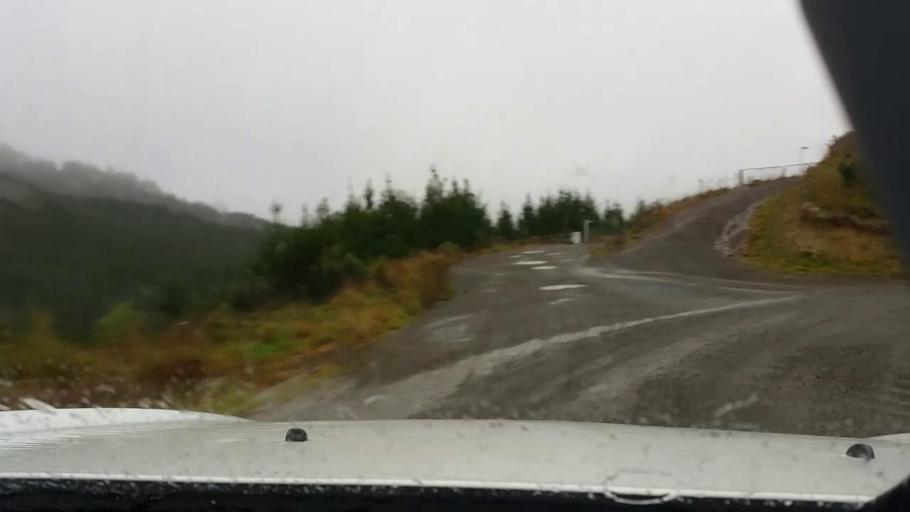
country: NZ
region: Wellington
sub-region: Masterton District
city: Masterton
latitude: -41.1957
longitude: 175.8106
